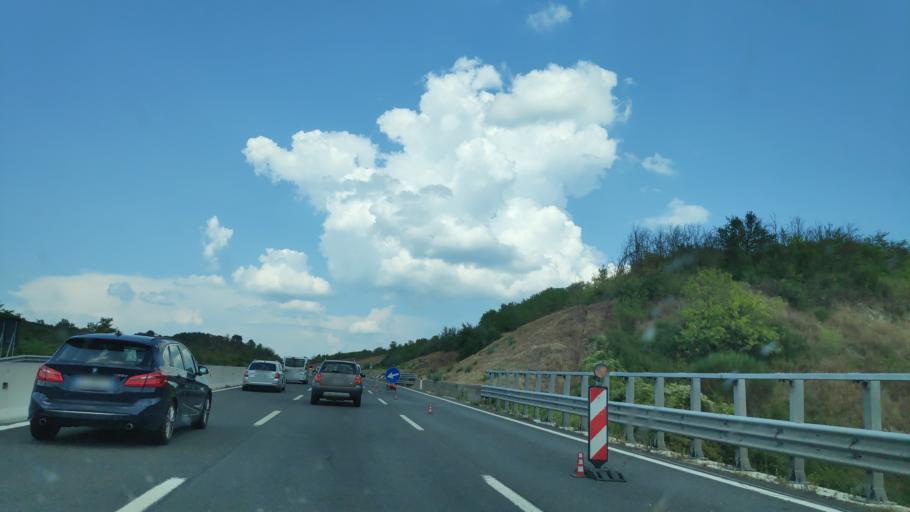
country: IT
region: Umbria
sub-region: Provincia di Terni
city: Ficulle
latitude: 42.8318
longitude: 12.0428
